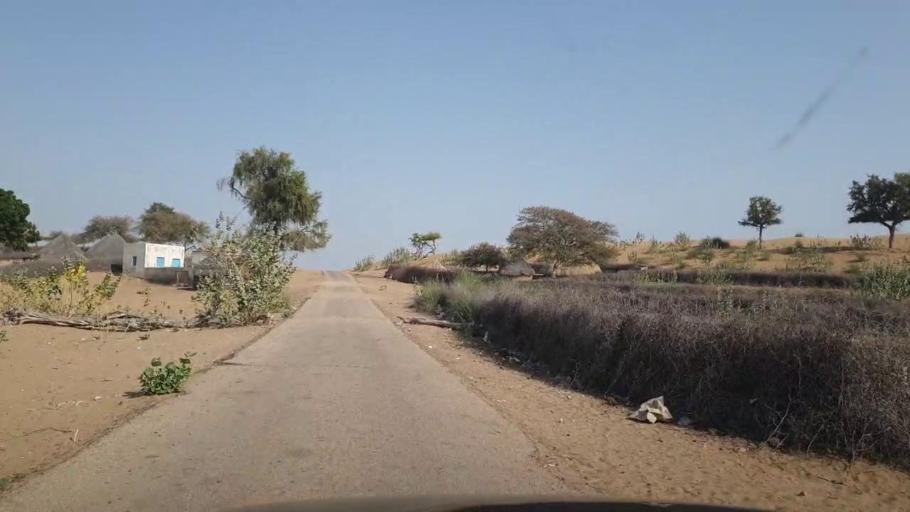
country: PK
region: Sindh
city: Islamkot
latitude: 25.1348
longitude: 70.4610
